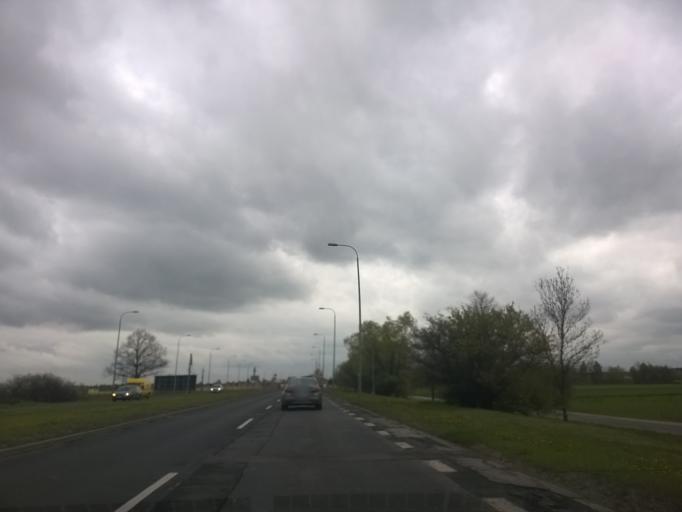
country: PL
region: Masovian Voivodeship
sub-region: Warszawa
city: Kabaty
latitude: 52.1400
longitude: 21.0979
